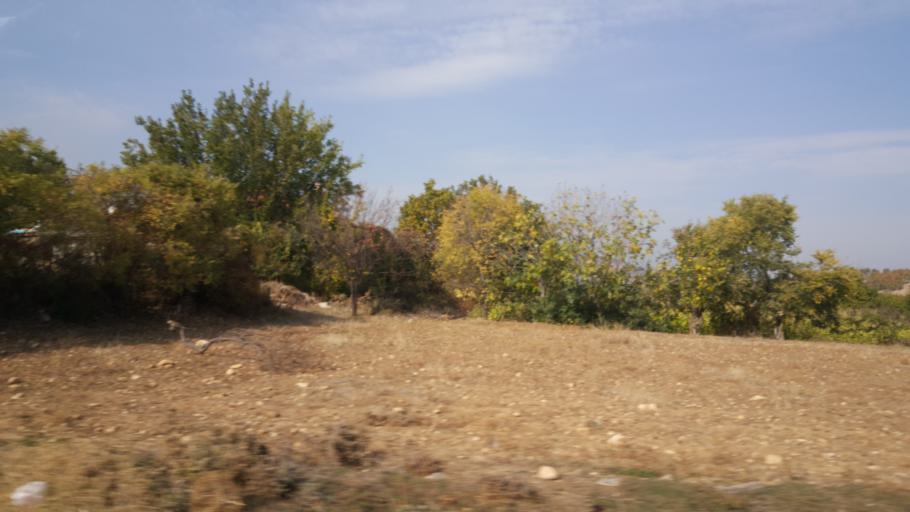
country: TR
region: Eskisehir
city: Mihaliccik
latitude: 39.9773
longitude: 31.3731
